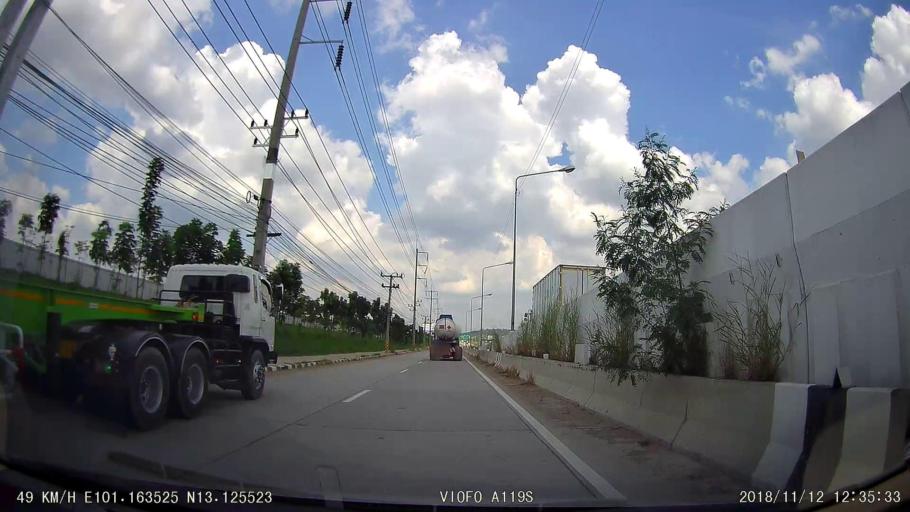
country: TH
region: Rayong
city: Pluak Daeng
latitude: 13.1256
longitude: 101.1636
